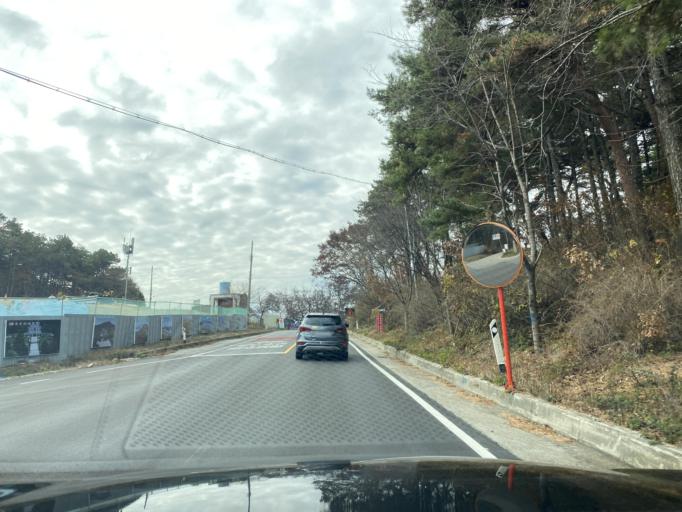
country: KR
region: Chungcheongnam-do
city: Hongsung
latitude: 36.6621
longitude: 126.6319
